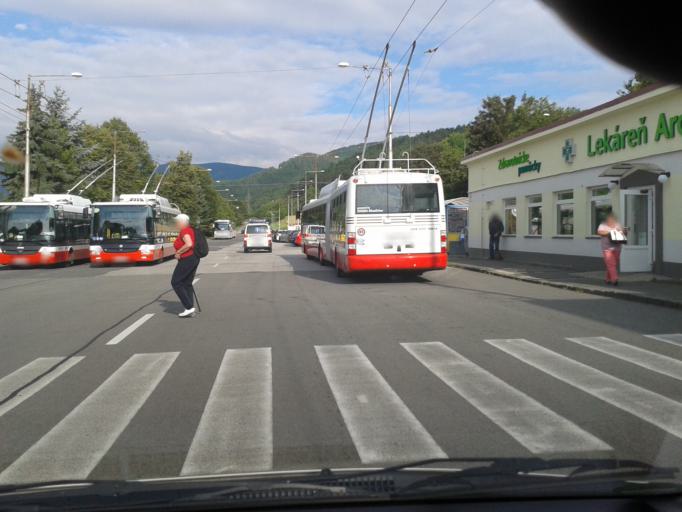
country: SK
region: Banskobystricky
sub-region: Okres Banska Bystrica
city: Banska Bystrica
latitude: 48.7444
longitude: 19.1192
